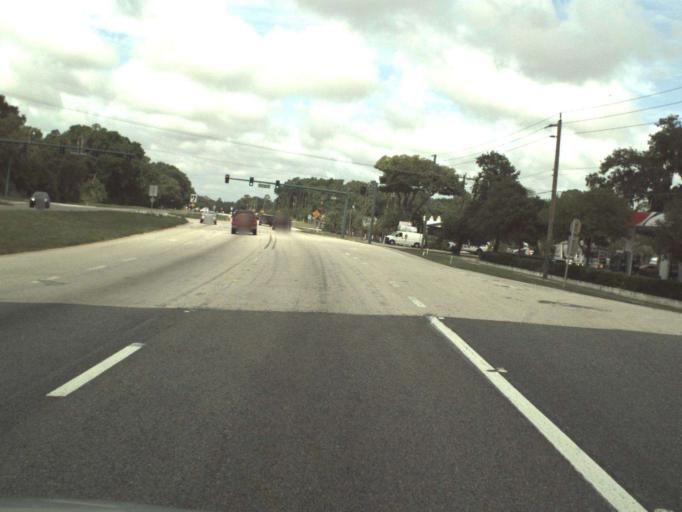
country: US
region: Florida
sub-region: Seminole County
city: Heathrow
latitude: 28.8119
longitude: -81.3617
